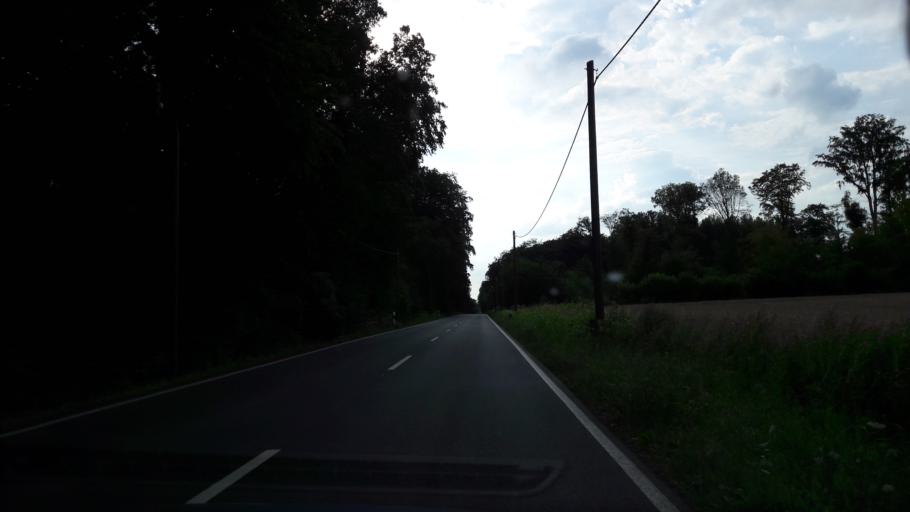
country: DE
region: North Rhine-Westphalia
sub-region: Regierungsbezirk Munster
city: Ennigerloh
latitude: 51.8101
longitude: 7.9906
